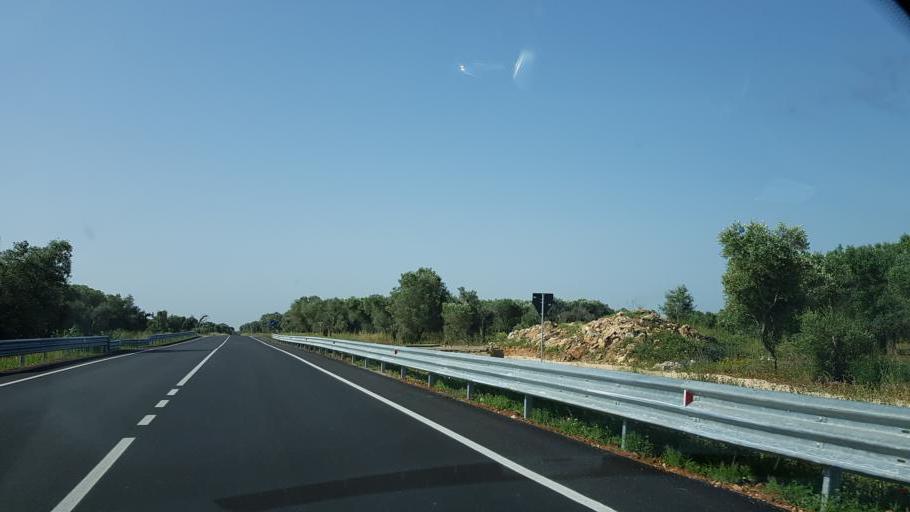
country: IT
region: Apulia
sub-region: Provincia di Brindisi
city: San Pancrazio Salentino
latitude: 40.4647
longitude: 17.8385
